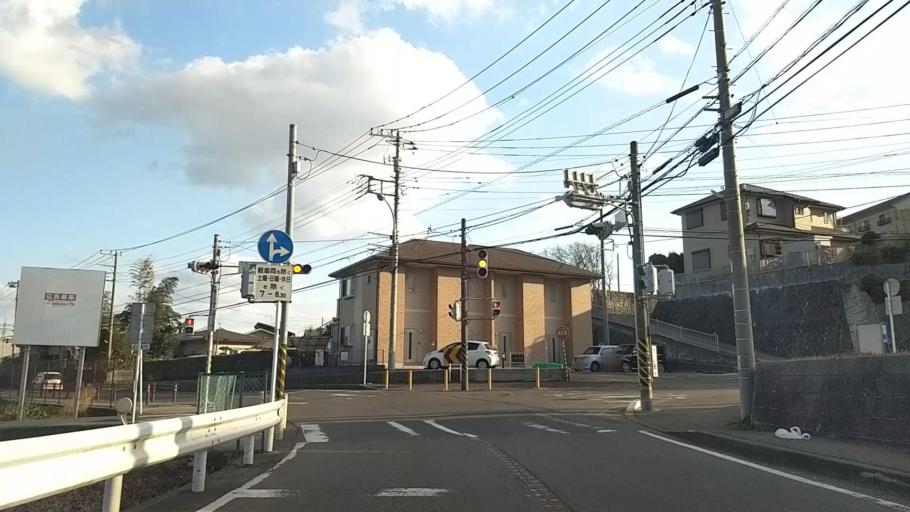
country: JP
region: Kanagawa
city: Atsugi
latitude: 35.4411
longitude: 139.3366
